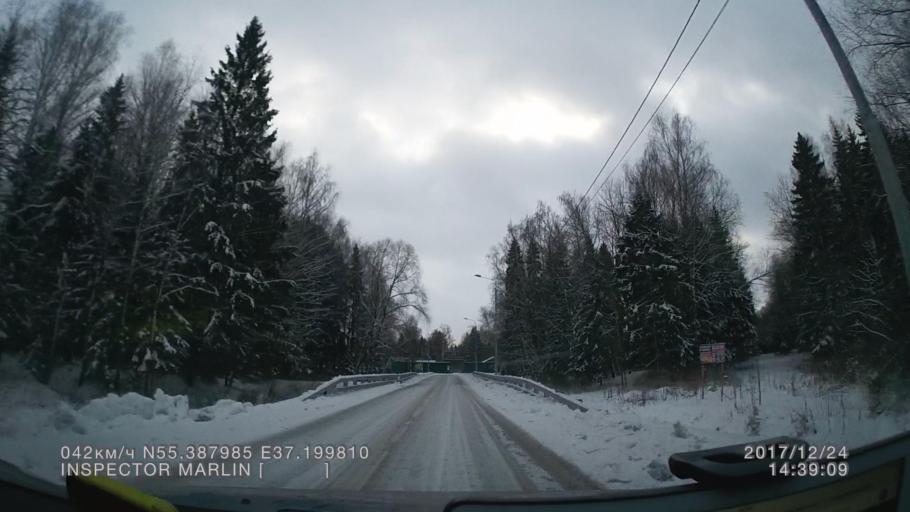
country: RU
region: Moskovskaya
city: Troitsk
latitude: 55.3878
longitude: 37.1998
